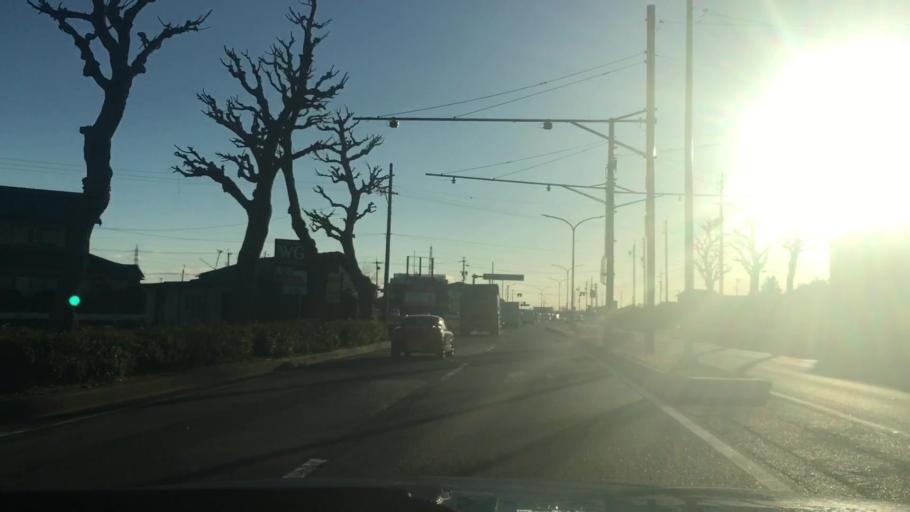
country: JP
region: Shizuoka
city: Hamamatsu
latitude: 34.7398
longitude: 137.6665
